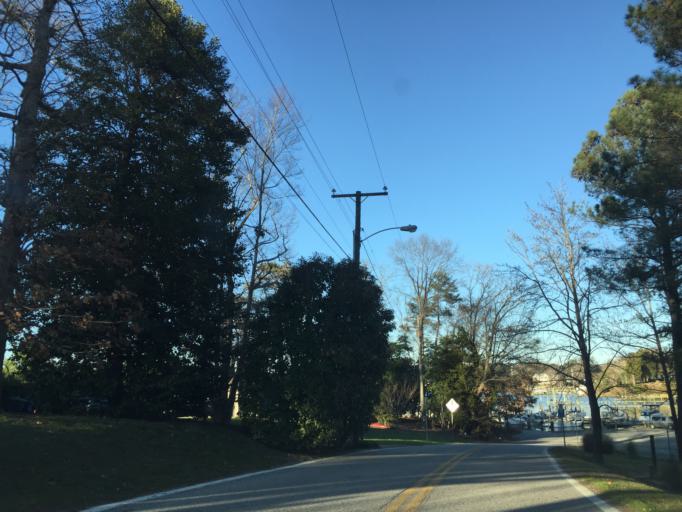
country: US
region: Virginia
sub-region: Isle of Wight County
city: Carrollton
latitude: 37.0794
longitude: -76.5238
